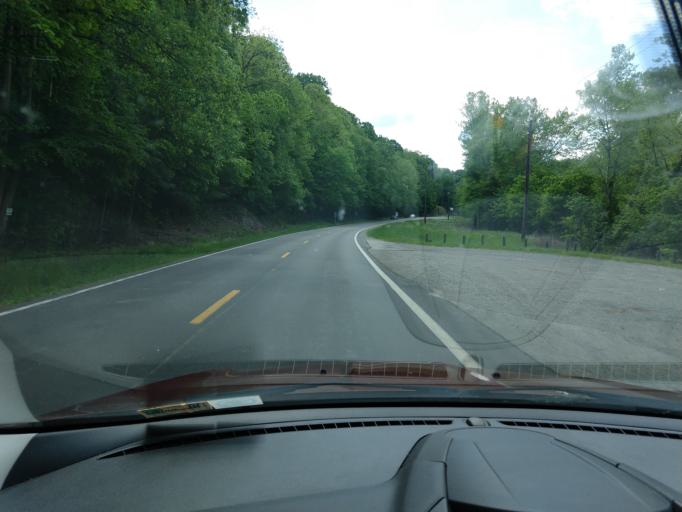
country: US
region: West Virginia
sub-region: Gilmer County
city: Glenville
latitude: 38.9155
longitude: -80.7664
